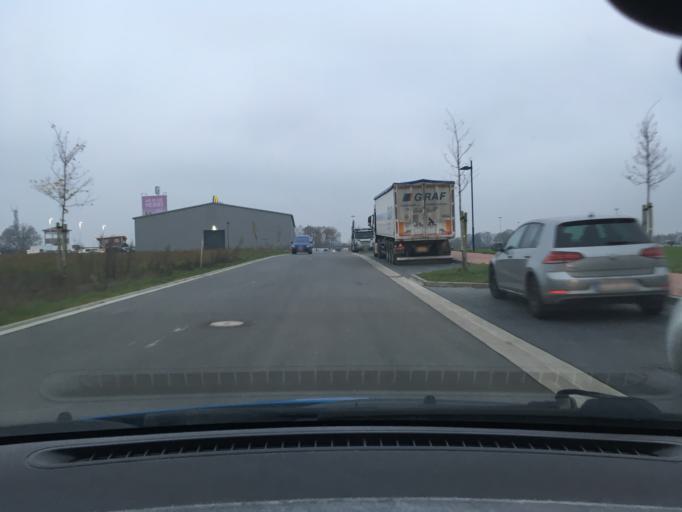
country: DE
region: Lower Saxony
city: Bispingen
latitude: 53.0998
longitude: 9.9837
